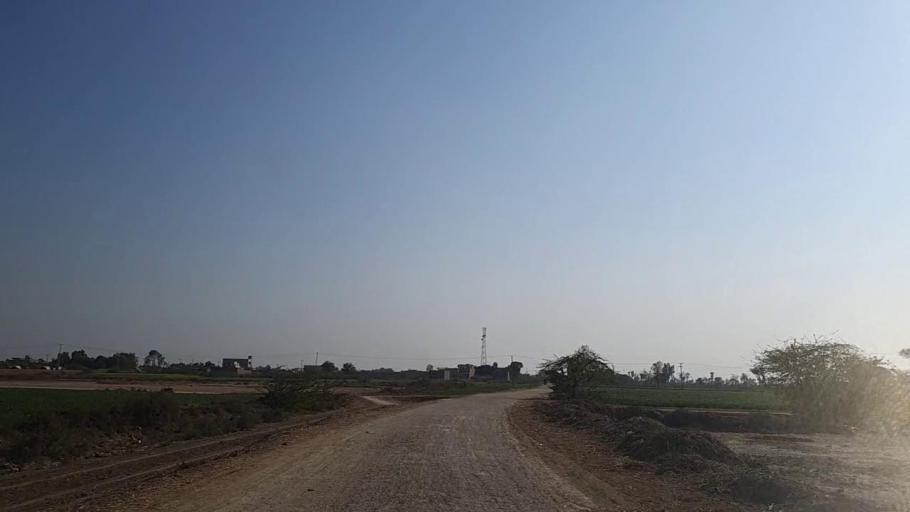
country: PK
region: Sindh
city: Daur
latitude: 26.4625
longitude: 68.3043
